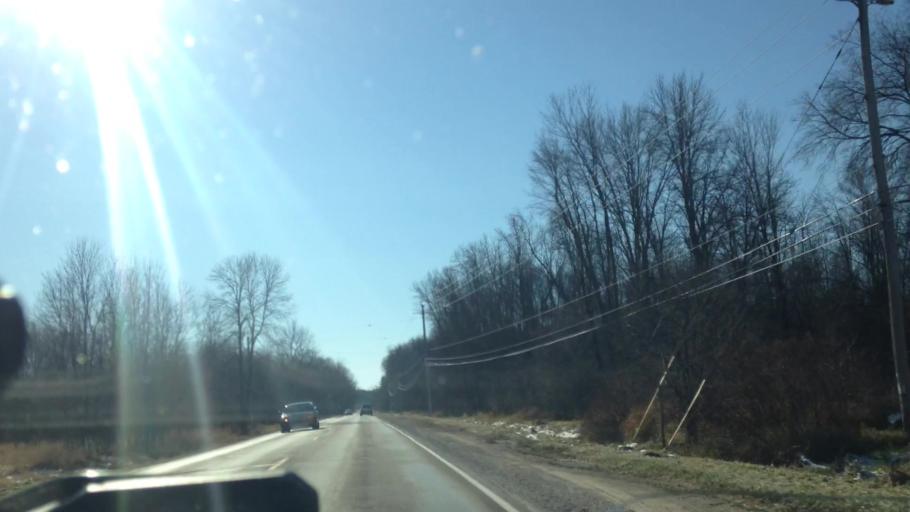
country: US
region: Wisconsin
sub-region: Waukesha County
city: Menomonee Falls
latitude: 43.2060
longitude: -88.1427
